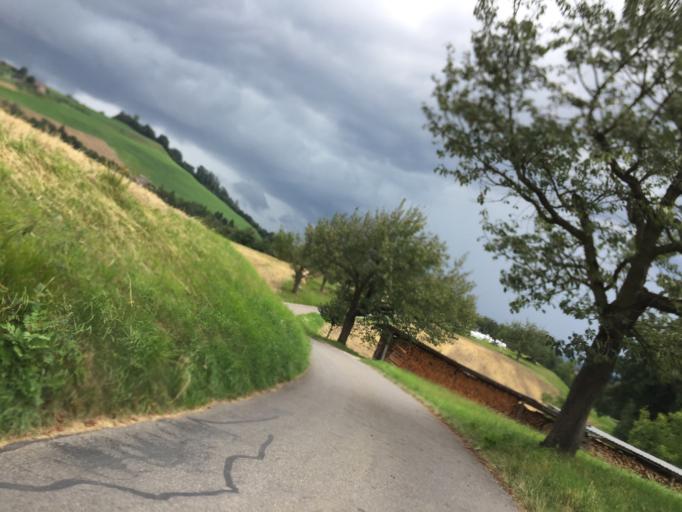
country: CH
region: Bern
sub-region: Bern-Mittelland District
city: Munsingen
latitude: 46.8600
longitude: 7.5463
